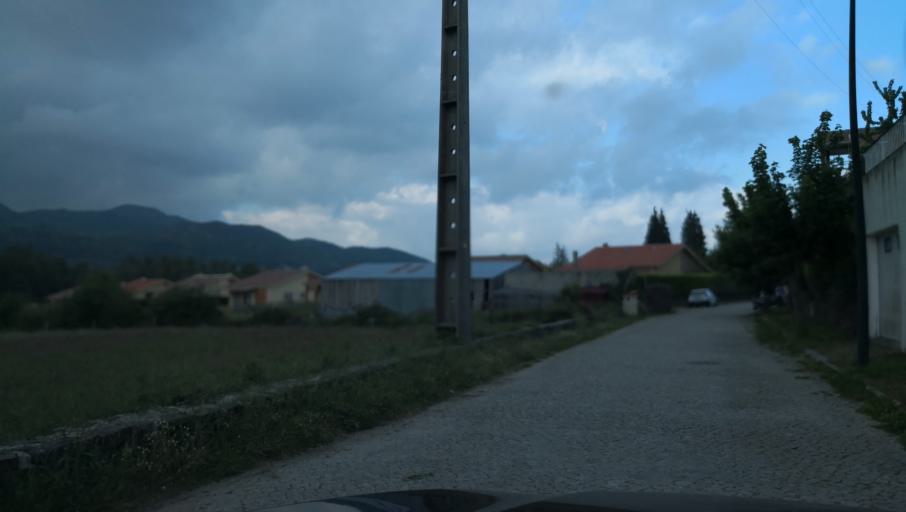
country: PT
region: Vila Real
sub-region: Santa Marta de Penaguiao
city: Santa Marta de Penaguiao
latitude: 41.2822
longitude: -7.8489
